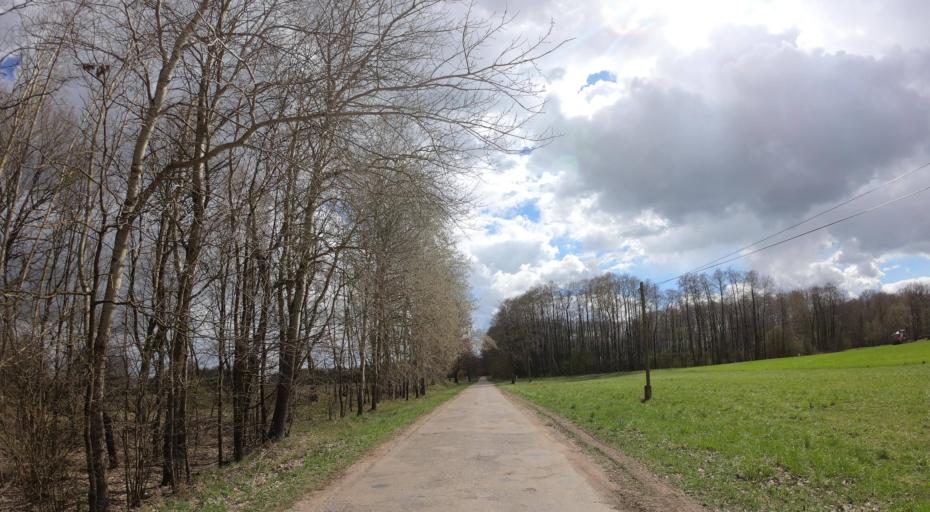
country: PL
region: West Pomeranian Voivodeship
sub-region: Powiat drawski
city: Drawsko Pomorskie
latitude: 53.5388
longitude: 15.8831
